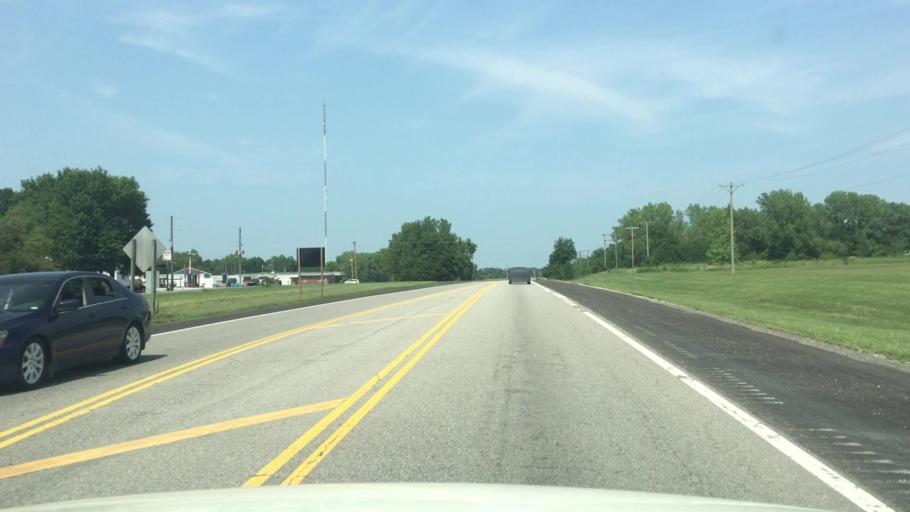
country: US
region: Kansas
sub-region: Crawford County
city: Pittsburg
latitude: 37.4275
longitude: -94.7150
